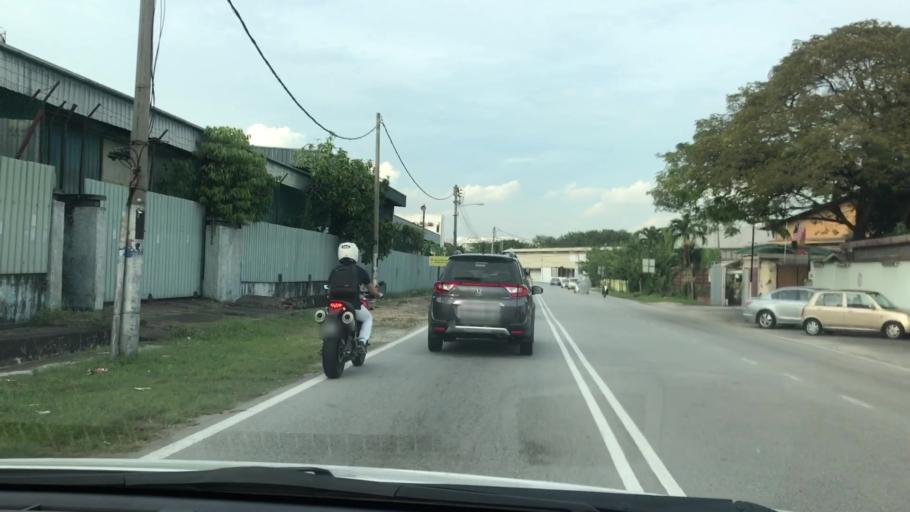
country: MY
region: Selangor
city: Kampong Baharu Balakong
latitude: 3.0139
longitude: 101.7016
